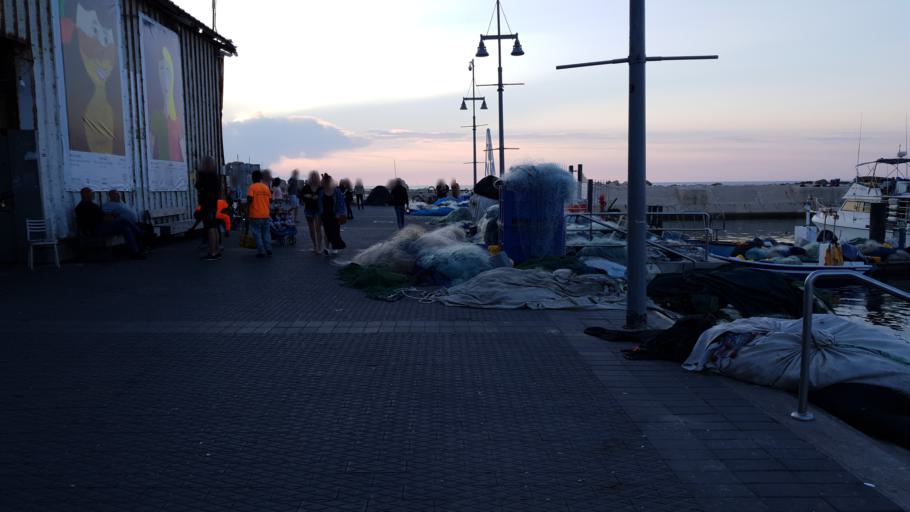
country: IL
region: Tel Aviv
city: Yafo
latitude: 32.0516
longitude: 34.7491
